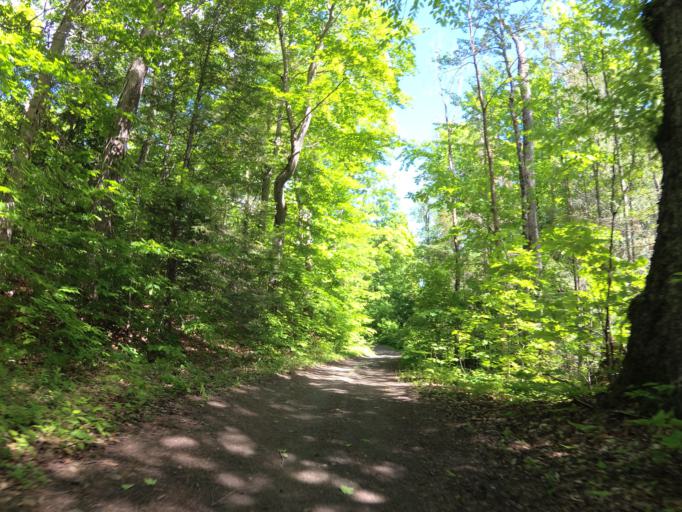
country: CA
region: Ontario
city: Renfrew
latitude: 45.0447
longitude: -76.8334
